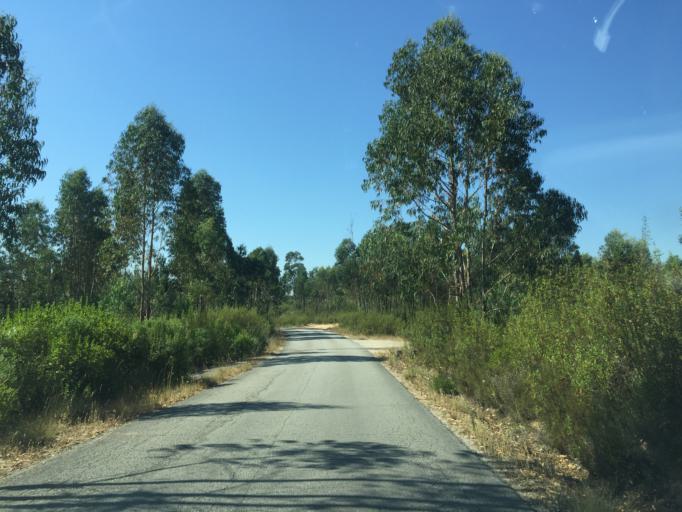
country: PT
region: Santarem
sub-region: Constancia
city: Constancia
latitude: 39.5623
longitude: -8.3213
